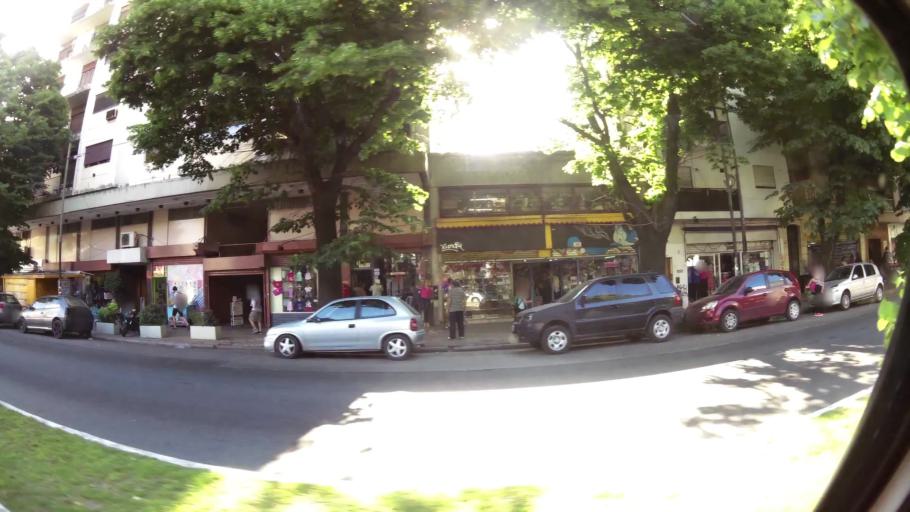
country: AR
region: Buenos Aires
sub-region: Partido de La Plata
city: La Plata
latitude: -34.9083
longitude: -57.9489
